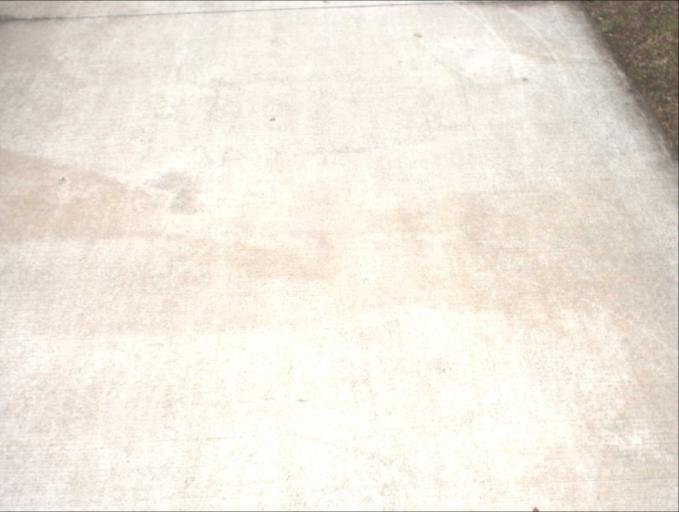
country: AU
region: Queensland
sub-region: Logan
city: Chambers Flat
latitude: -27.8007
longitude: 153.1078
